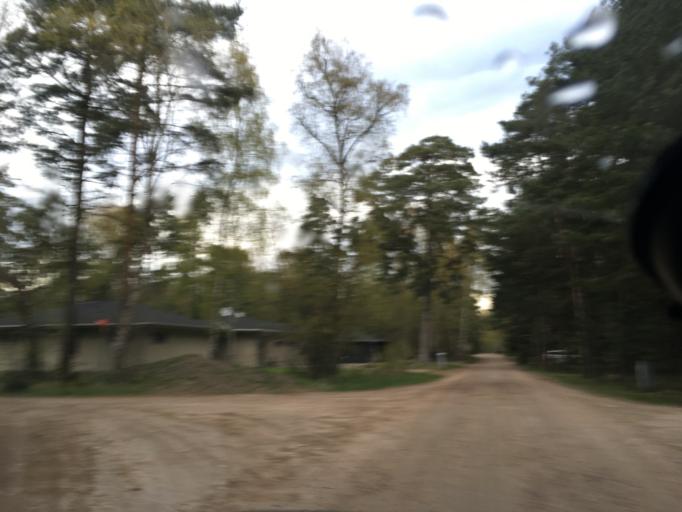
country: SE
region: Skane
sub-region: Vellinge Kommun
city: Ljunghusen
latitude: 55.4027
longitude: 12.9262
